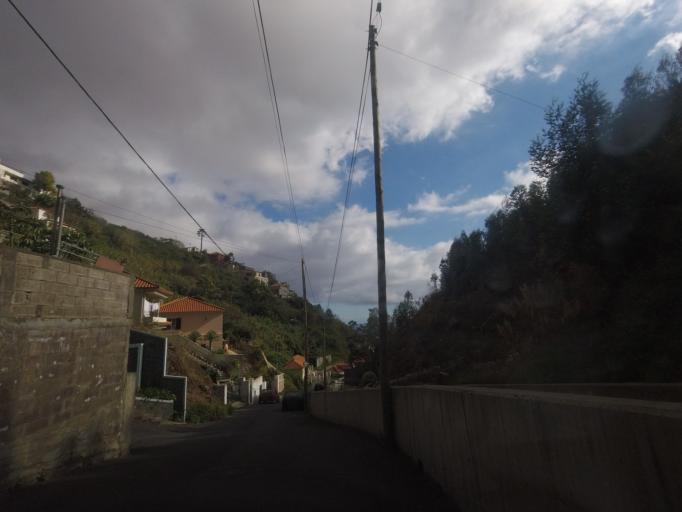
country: PT
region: Madeira
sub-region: Funchal
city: Nossa Senhora do Monte
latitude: 32.6756
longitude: -16.9313
